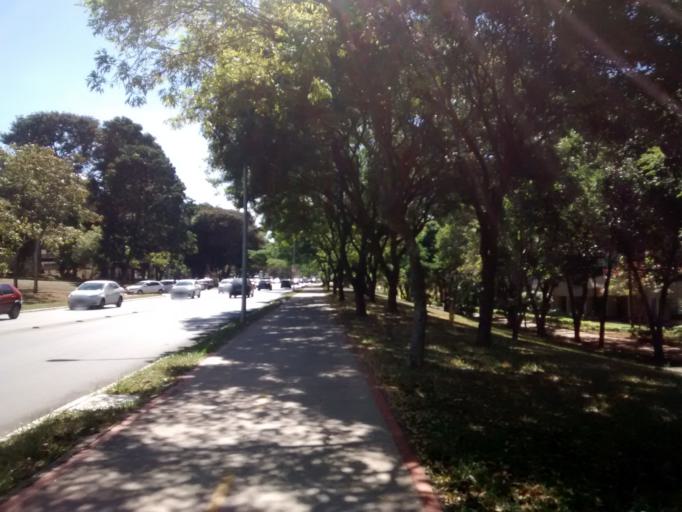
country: BR
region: Federal District
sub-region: Brasilia
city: Brasilia
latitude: -15.7518
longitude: -47.8910
